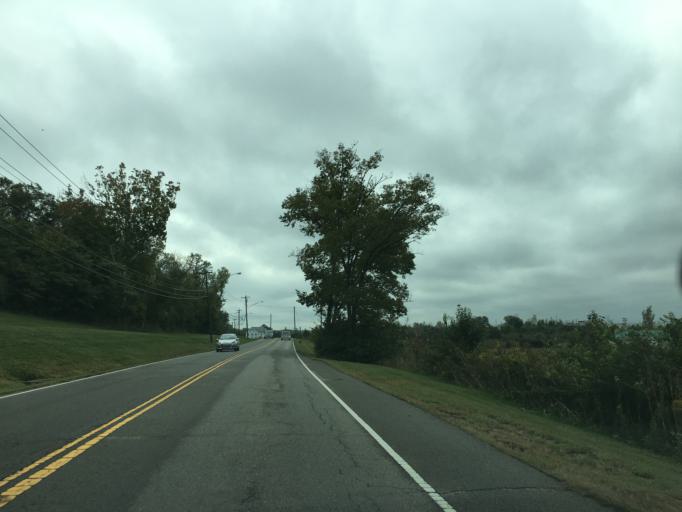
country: US
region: Ohio
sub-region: Butler County
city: Beckett Ridge
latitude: 39.3475
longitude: -84.4476
